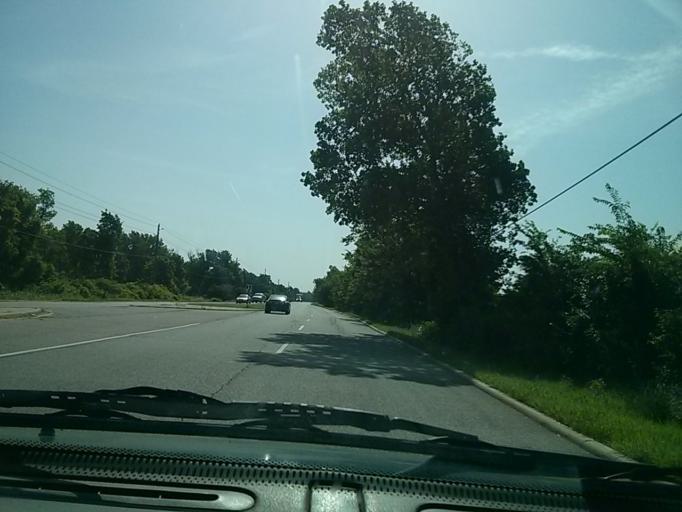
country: US
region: Oklahoma
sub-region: Tulsa County
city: Broken Arrow
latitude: 36.1334
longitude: -95.8137
